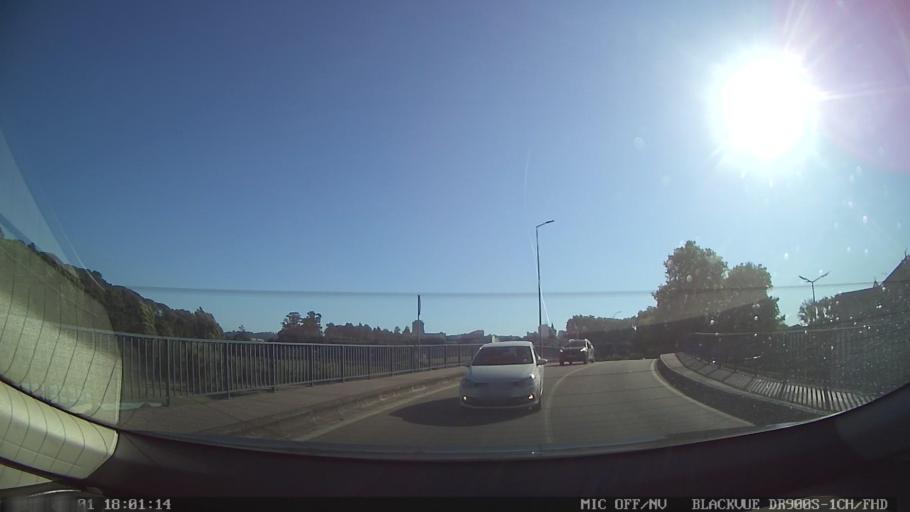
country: PT
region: Porto
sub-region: Santo Tirso
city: Santo Tirso
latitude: 41.3470
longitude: -8.4680
